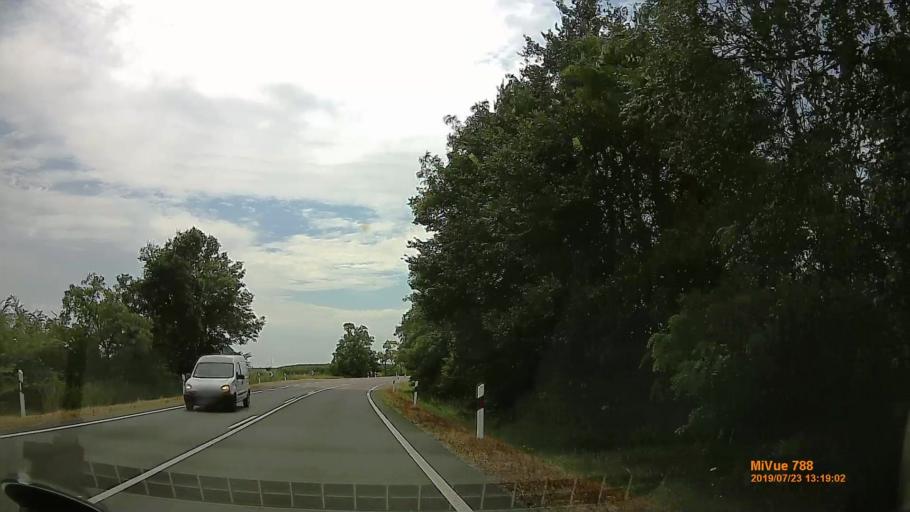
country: HU
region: Hajdu-Bihar
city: Polgar
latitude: 47.8777
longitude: 21.1448
